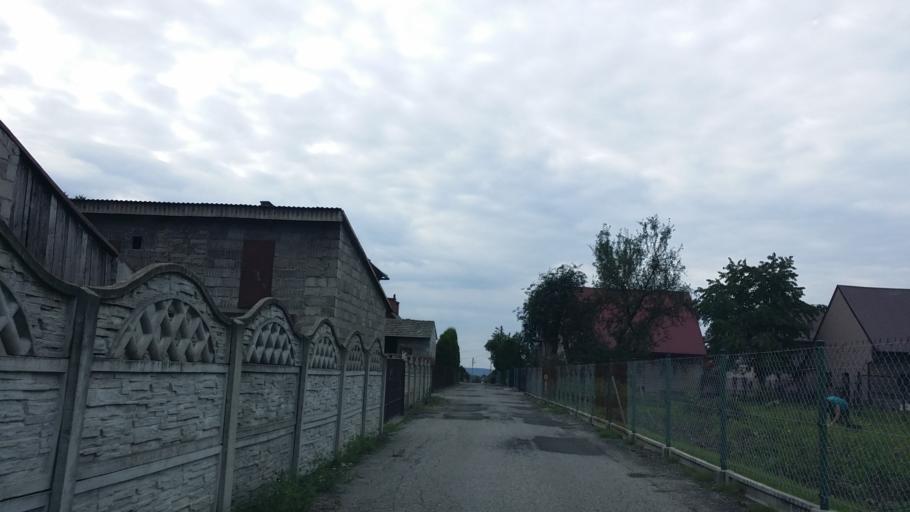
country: PL
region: Lesser Poland Voivodeship
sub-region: Powiat wadowicki
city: Spytkowice
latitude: 49.9990
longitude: 19.5175
